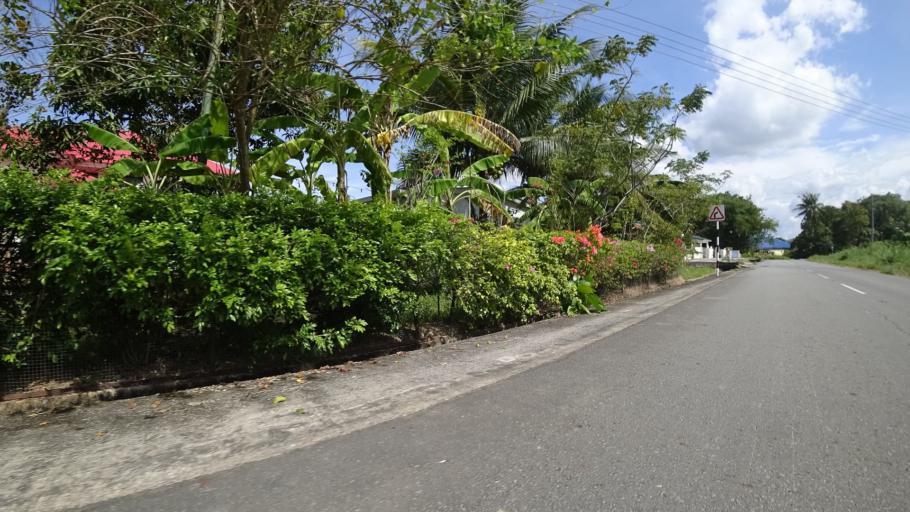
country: BN
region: Brunei and Muara
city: Bandar Seri Begawan
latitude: 4.8901
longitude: 114.8490
